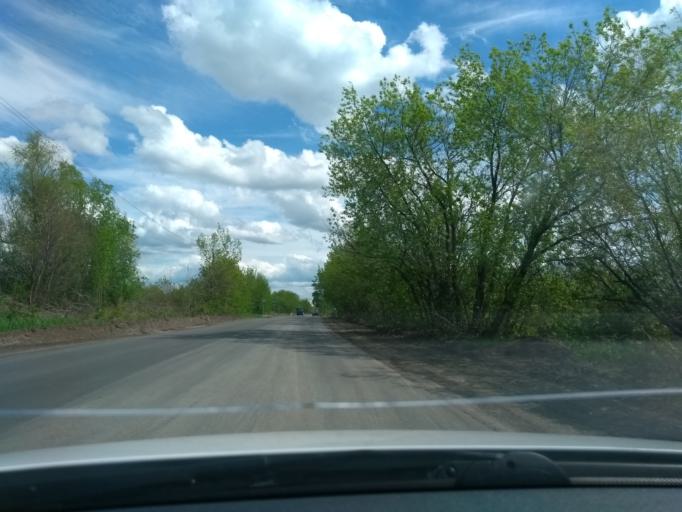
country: RU
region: Perm
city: Kondratovo
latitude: 58.0096
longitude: 56.0802
